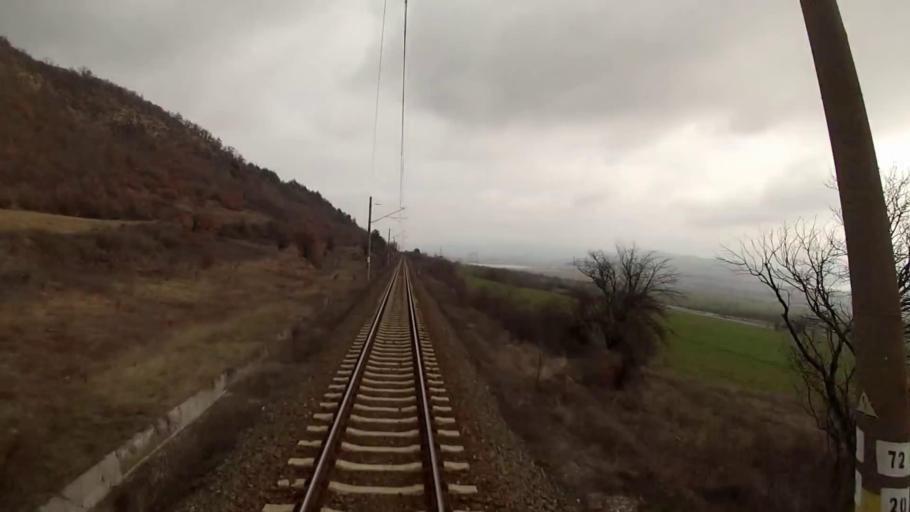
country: BG
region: Sofiya
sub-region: Obshtina Chelopech
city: Chelopech
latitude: 42.6915
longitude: 24.0561
